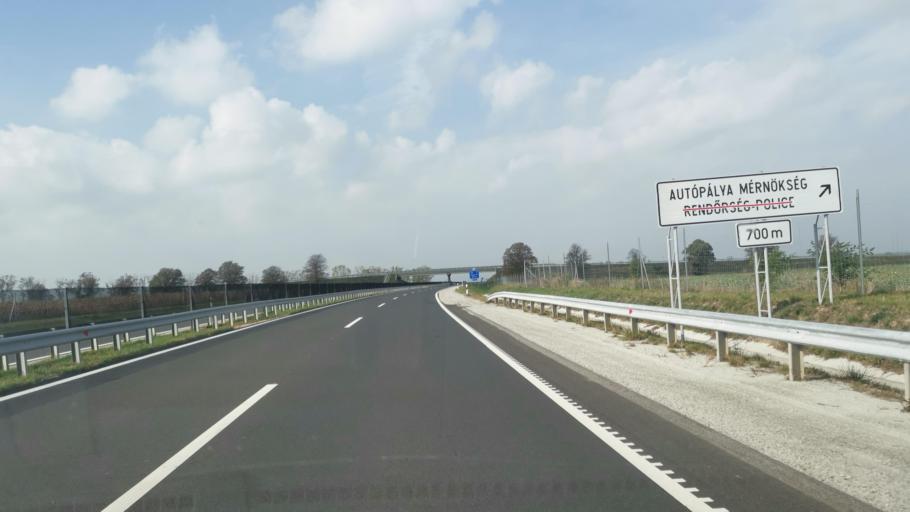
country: HU
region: Gyor-Moson-Sopron
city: Nagycenk
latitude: 47.5835
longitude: 16.7210
